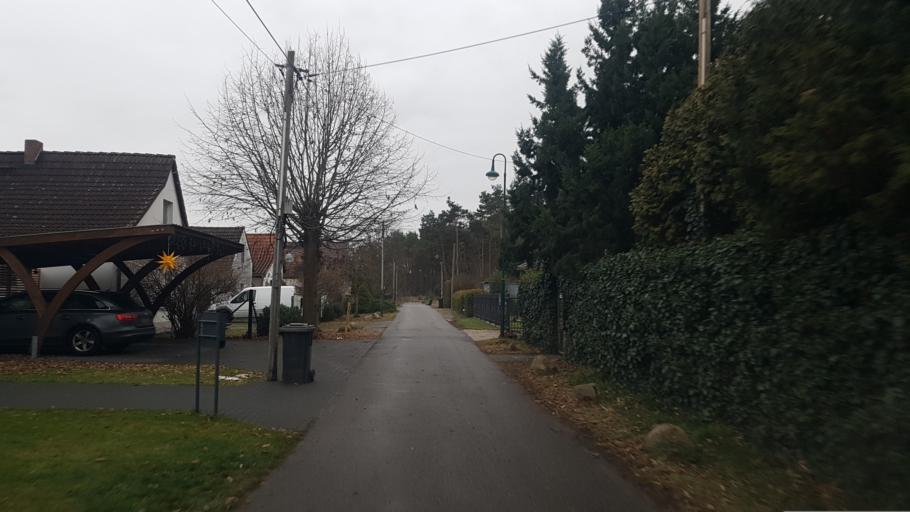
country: DE
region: Brandenburg
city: Cottbus
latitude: 51.6966
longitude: 14.4238
